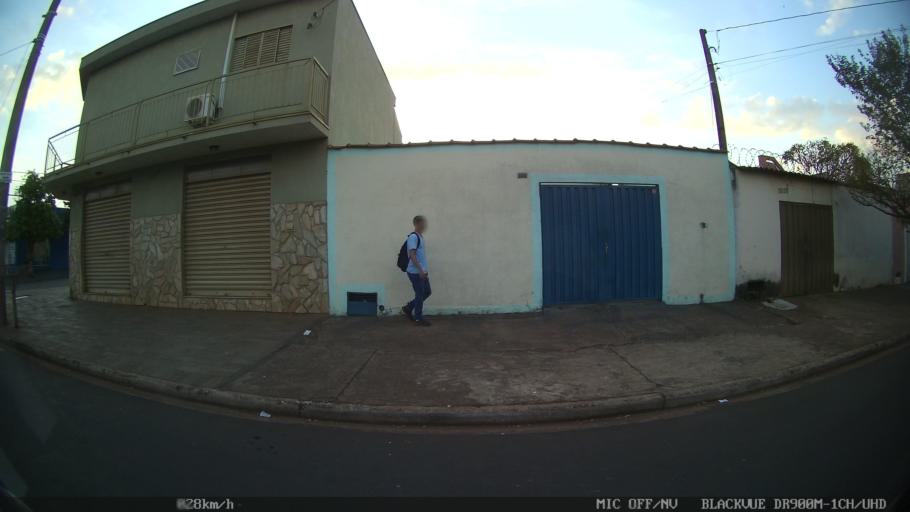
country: BR
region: Sao Paulo
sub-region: Ribeirao Preto
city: Ribeirao Preto
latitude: -21.1317
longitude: -47.8145
